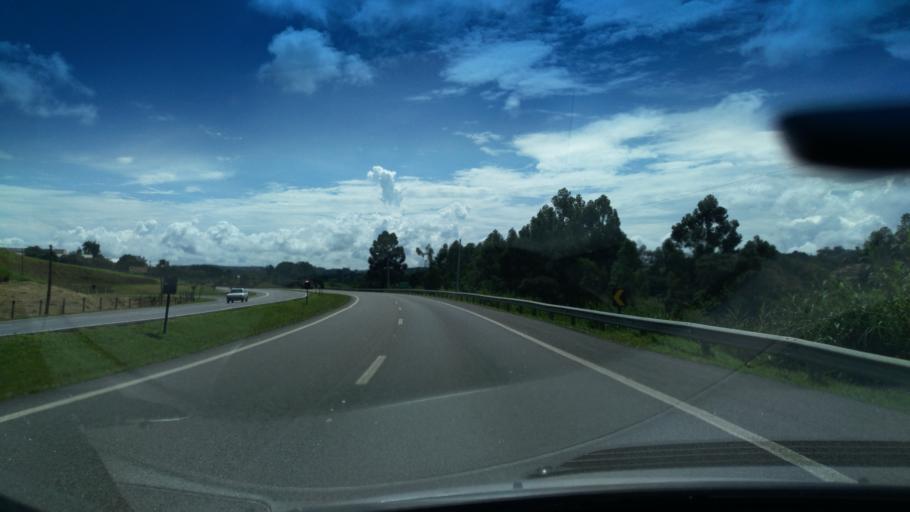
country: BR
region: Sao Paulo
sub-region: Santo Antonio Do Jardim
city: Espirito Santo do Pinhal
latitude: -22.2065
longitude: -46.7783
